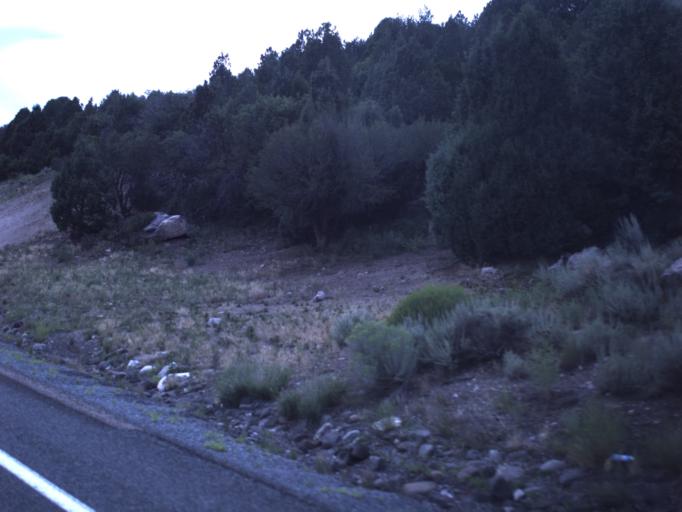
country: US
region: Utah
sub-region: Garfield County
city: Panguitch
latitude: 38.0279
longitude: -112.5312
